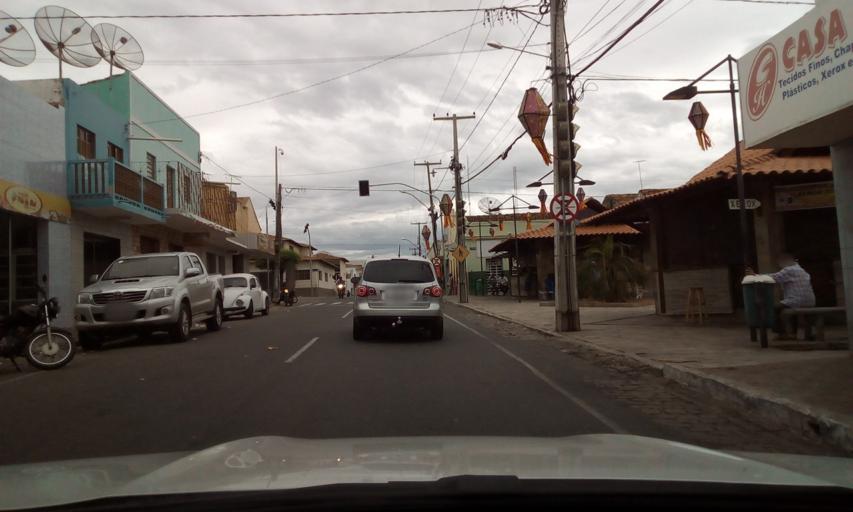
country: BR
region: Paraiba
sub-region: Picui
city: Picui
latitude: -6.5099
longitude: -36.3461
